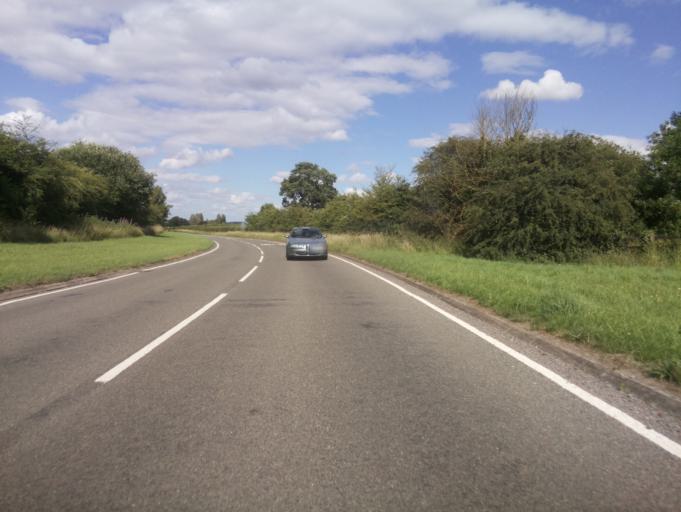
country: GB
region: England
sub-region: Leicestershire
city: Shepshed
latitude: 52.7960
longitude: -1.2887
